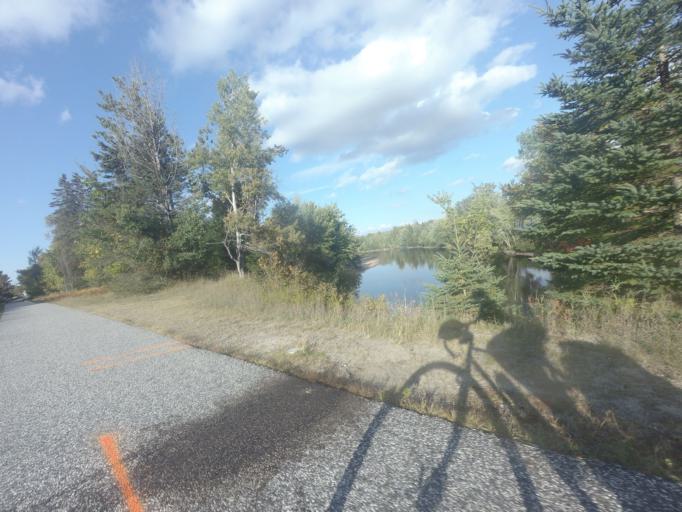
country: CA
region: Quebec
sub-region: Laurentides
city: Riviere-Rouge
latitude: 46.4104
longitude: -74.8697
